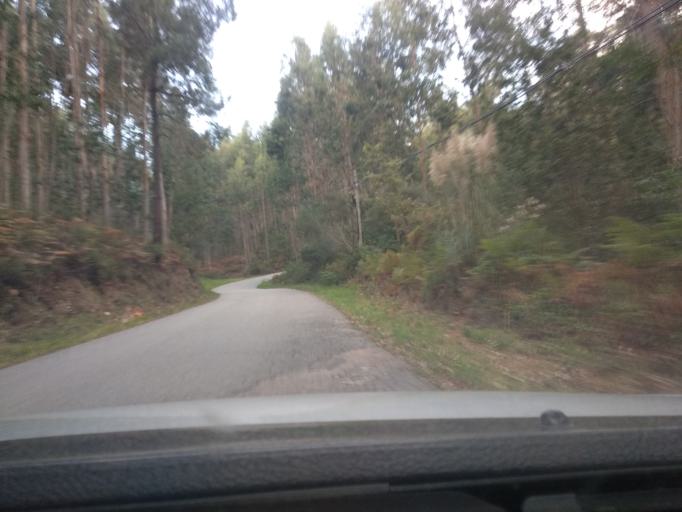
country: ES
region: Galicia
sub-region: Provincia de Pontevedra
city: Moana
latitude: 42.2946
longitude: -8.6941
